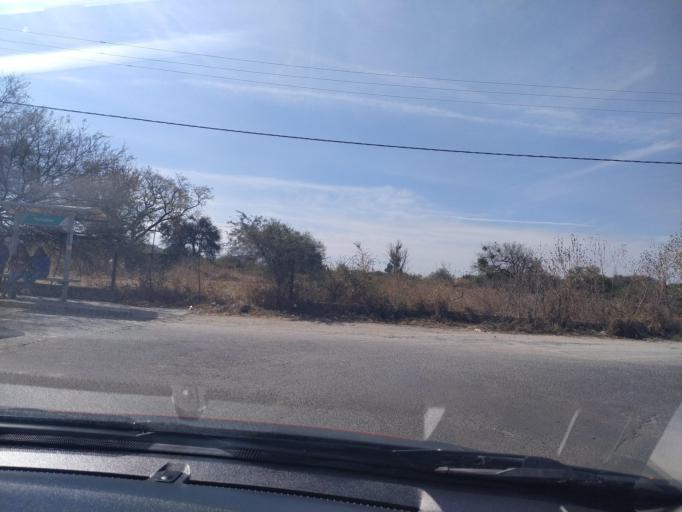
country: MX
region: Guanajuato
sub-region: San Francisco del Rincon
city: San Ignacio de Hidalgo
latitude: 20.8815
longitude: -101.8581
